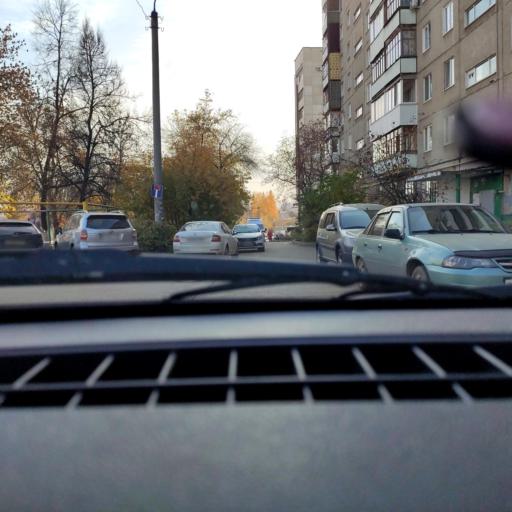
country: RU
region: Bashkortostan
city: Ufa
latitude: 54.7475
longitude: 55.9985
